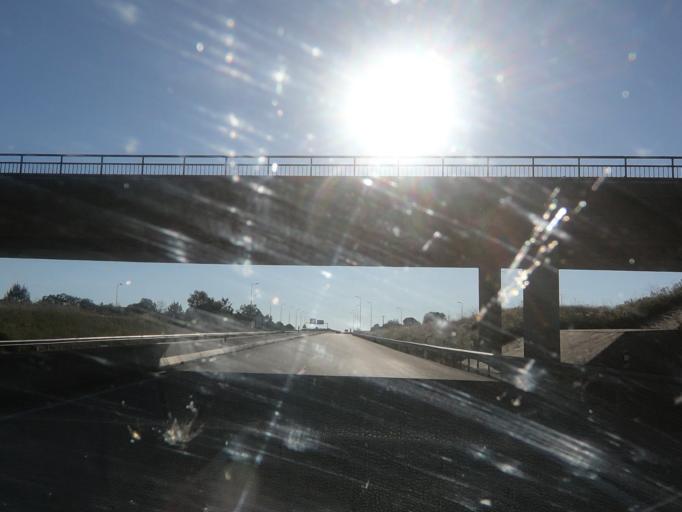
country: ES
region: Castille and Leon
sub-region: Provincia de Salamanca
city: Fuentes de Onoro
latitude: 40.6075
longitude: -6.9824
